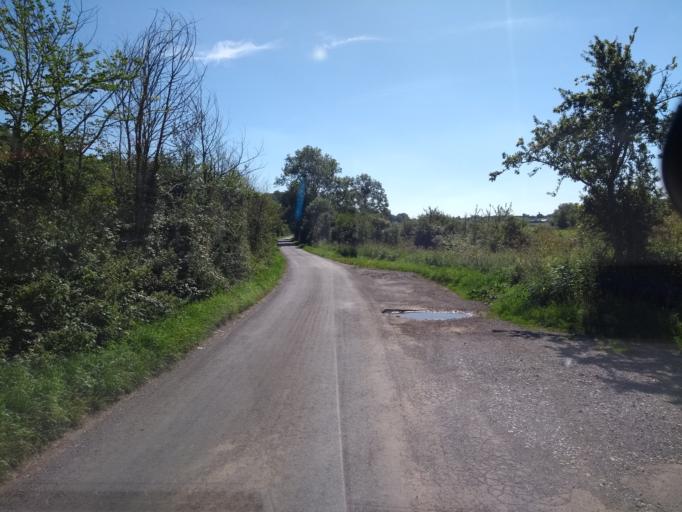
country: GB
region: England
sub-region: Somerset
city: Ilchester
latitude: 51.0557
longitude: -2.6919
